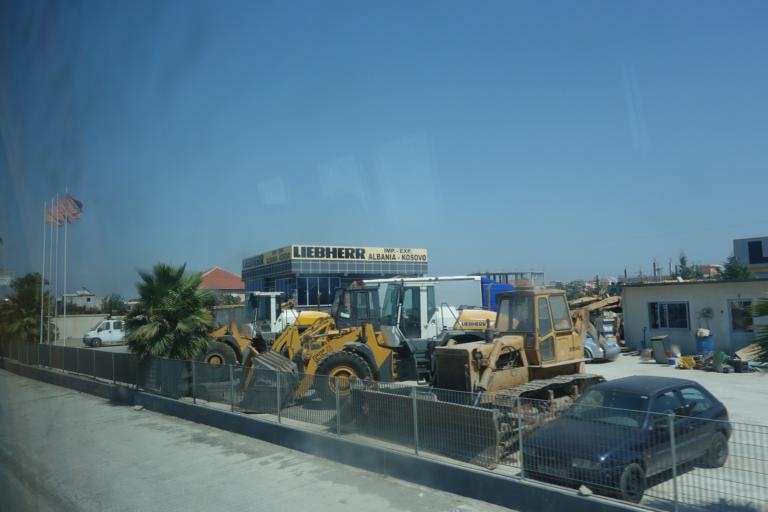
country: AL
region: Durres
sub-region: Rrethi i Durresit
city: Rrashbull
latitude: 41.3366
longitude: 19.4842
